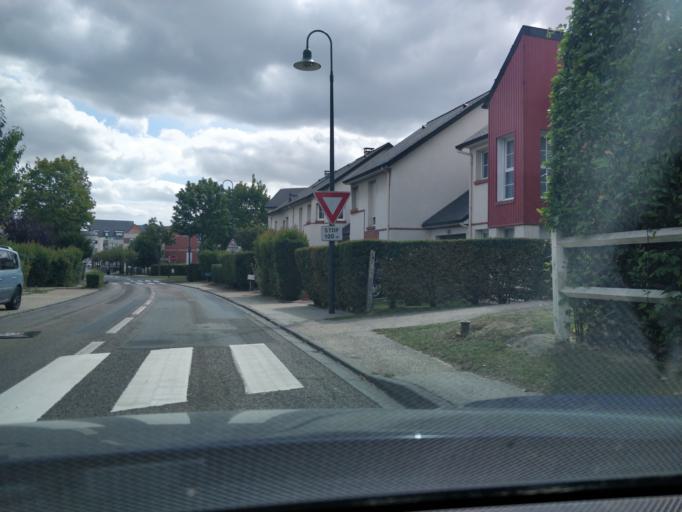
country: FR
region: Haute-Normandie
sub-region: Departement de la Seine-Maritime
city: Bois-Guillaume
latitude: 49.4808
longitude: 1.1104
